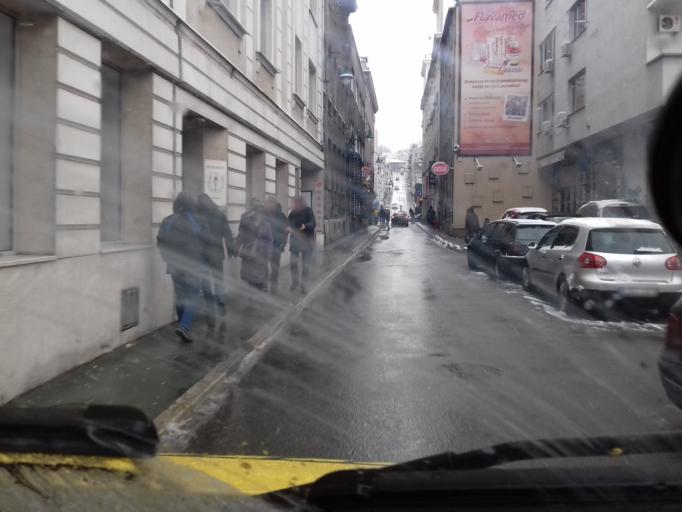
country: BA
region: Federation of Bosnia and Herzegovina
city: Kobilja Glava
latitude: 43.8581
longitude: 18.4204
